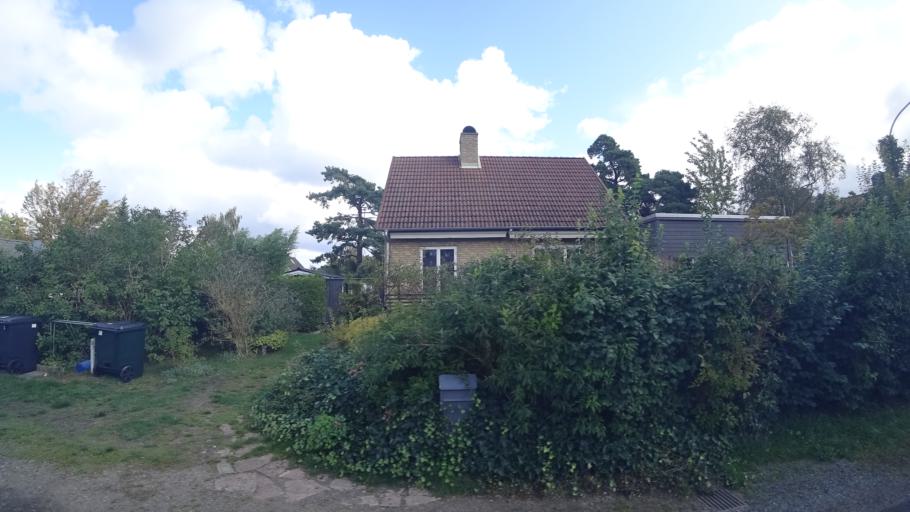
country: SE
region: Skane
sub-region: Kristianstads Kommun
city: Ahus
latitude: 55.9317
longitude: 14.3065
